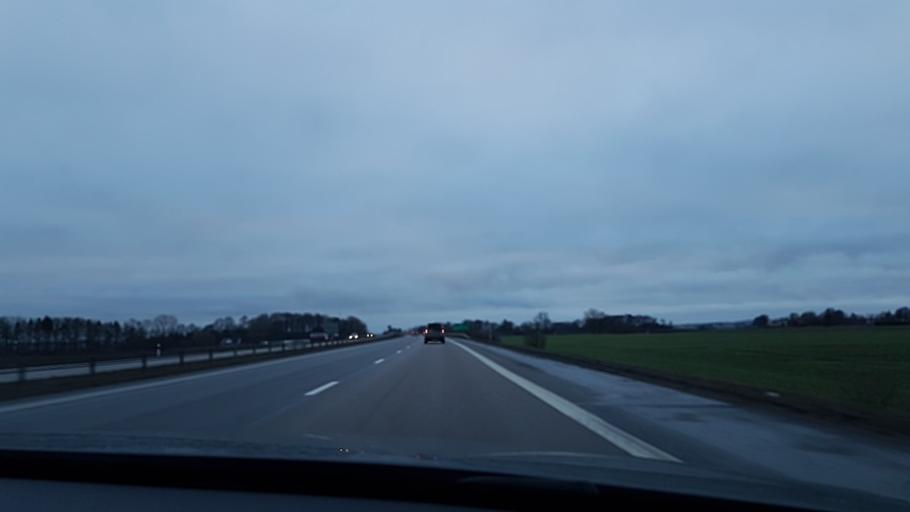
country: SE
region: Skane
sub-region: Astorps Kommun
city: Kvidinge
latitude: 56.1892
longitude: 13.0488
